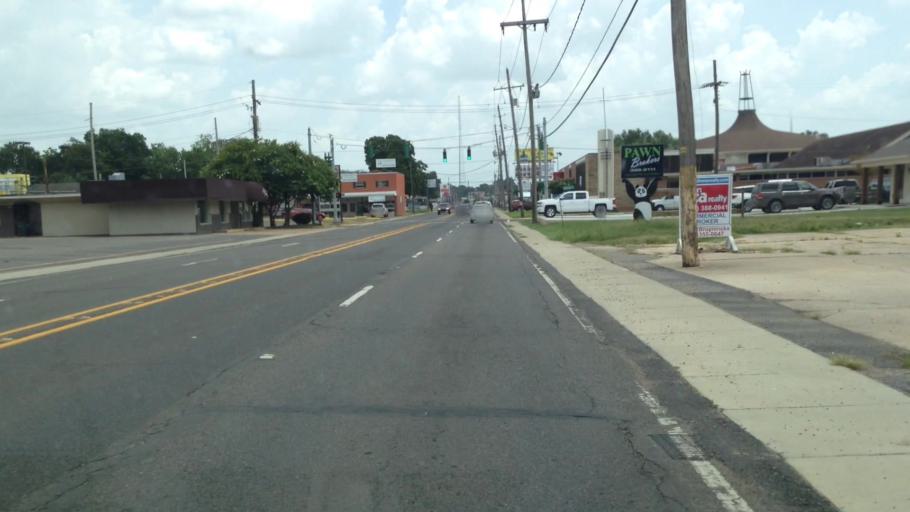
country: US
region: Louisiana
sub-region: Ouachita Parish
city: Monroe
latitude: 32.5071
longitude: -92.1313
